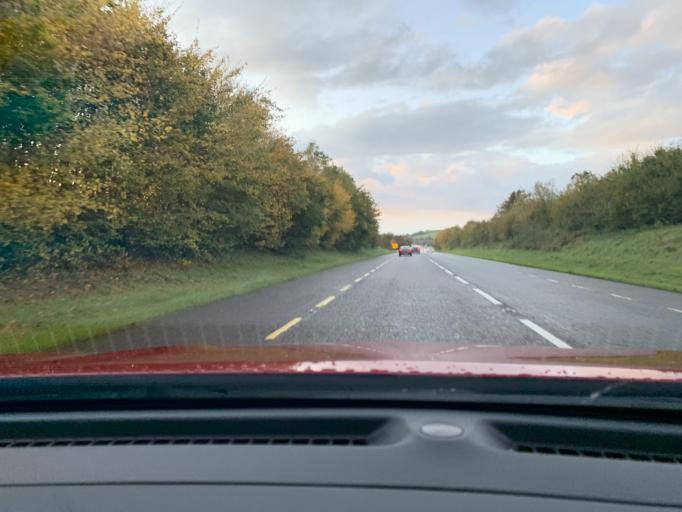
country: IE
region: Connaught
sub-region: Roscommon
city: Boyle
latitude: 54.0679
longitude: -8.3618
